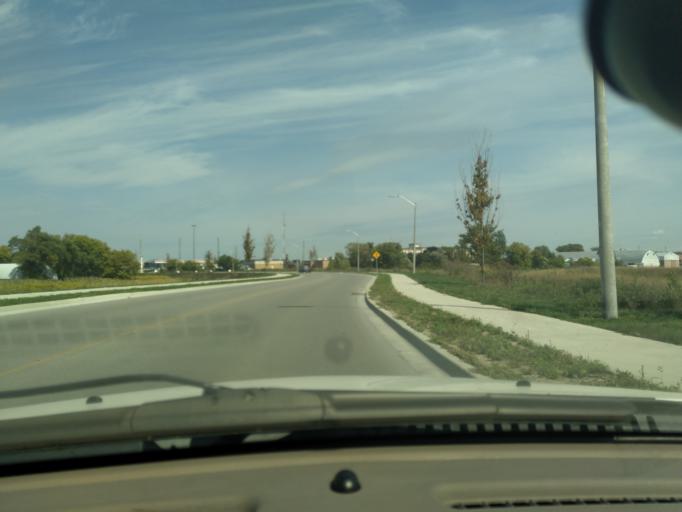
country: CA
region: Ontario
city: Bradford West Gwillimbury
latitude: 44.1132
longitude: -79.5585
